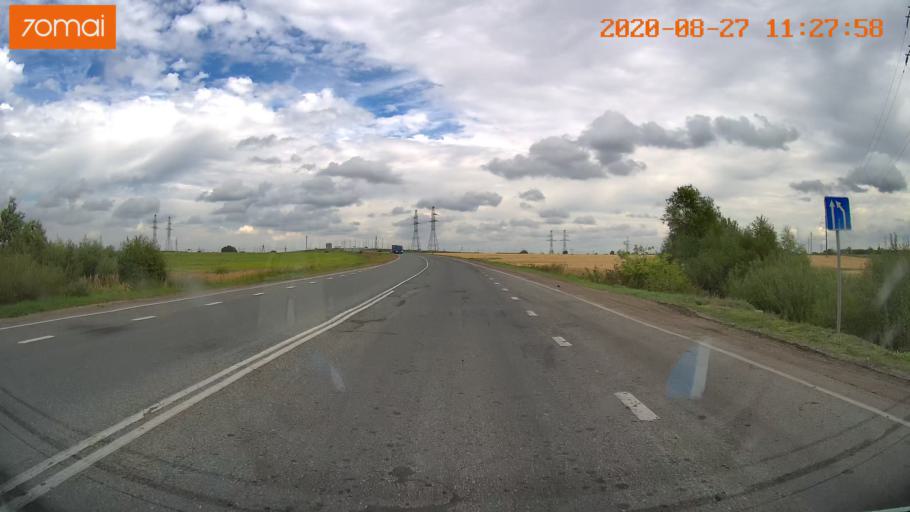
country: RU
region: Rjazan
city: Mikhaylov
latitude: 54.2556
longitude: 38.9990
